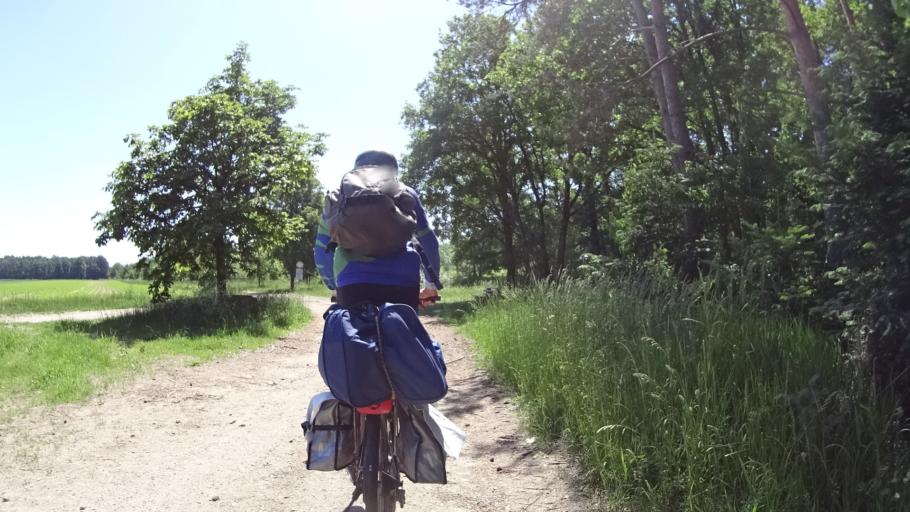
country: DE
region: Bavaria
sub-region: Regierungsbezirk Mittelfranken
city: Pfofeld
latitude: 49.1219
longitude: 10.8395
